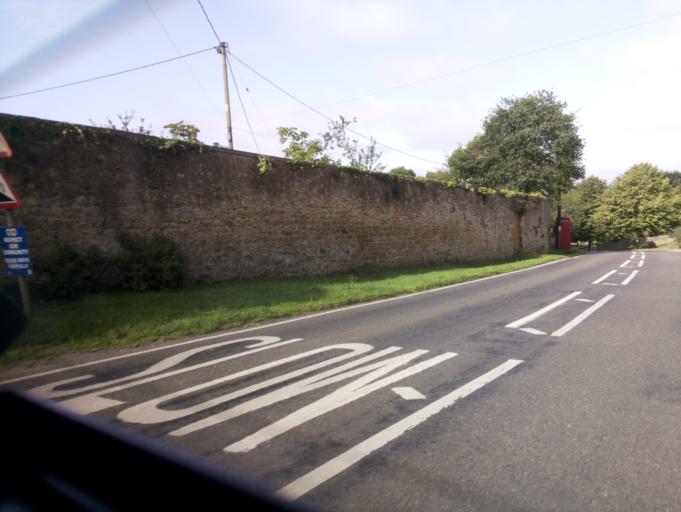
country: GB
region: England
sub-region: Oxfordshire
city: Shrivenham
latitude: 51.6422
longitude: -1.6594
